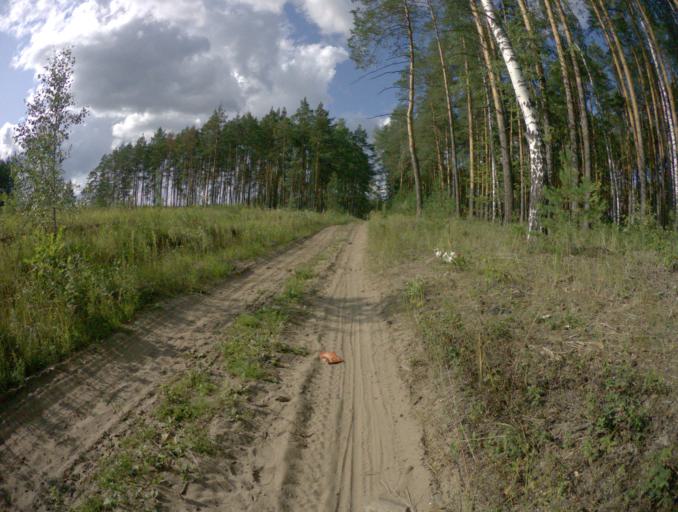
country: RU
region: Vladimir
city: Sobinka
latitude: 55.9591
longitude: 40.0608
